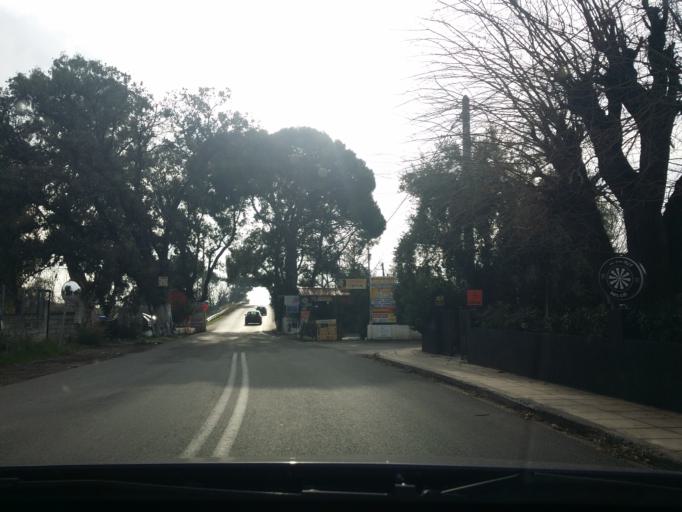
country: GR
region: Attica
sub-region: Nomarchia Anatolikis Attikis
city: Varybobi
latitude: 38.1003
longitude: 23.7793
